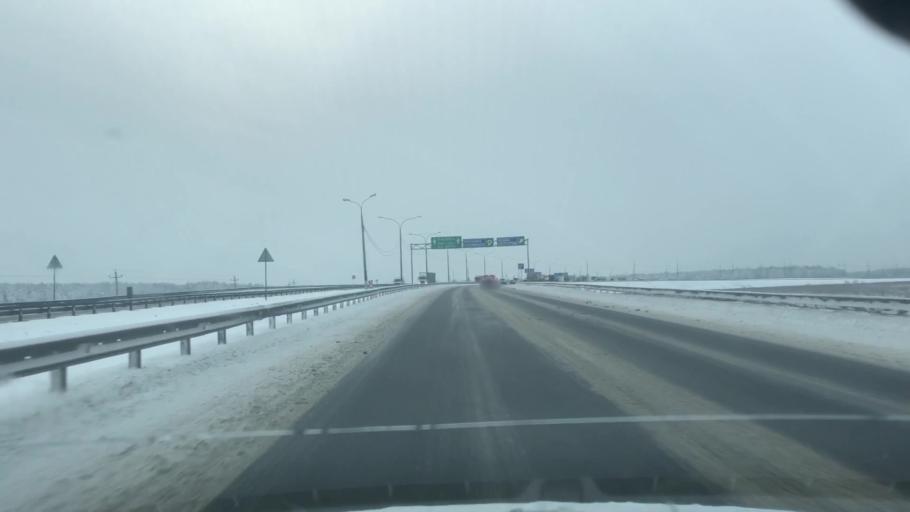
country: RU
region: Moskovskaya
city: Mikhnevo
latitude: 55.0826
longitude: 37.9354
